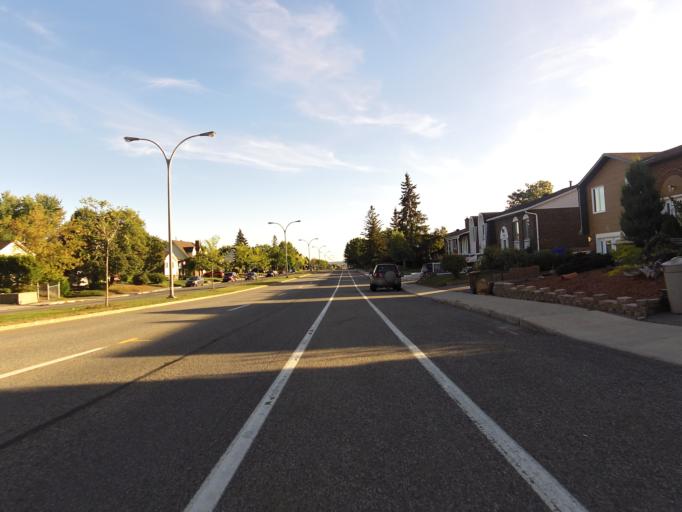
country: CA
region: Ontario
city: Bells Corners
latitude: 45.4076
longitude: -75.8387
